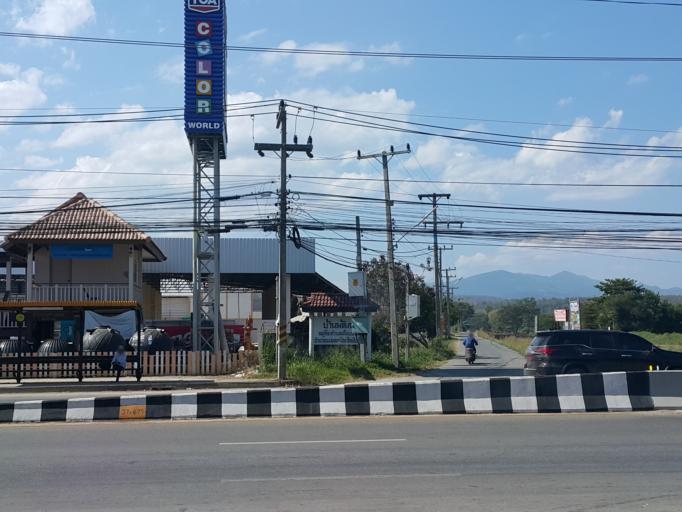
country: TH
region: Chiang Mai
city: Mae Taeng
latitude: 19.1016
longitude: 98.9363
